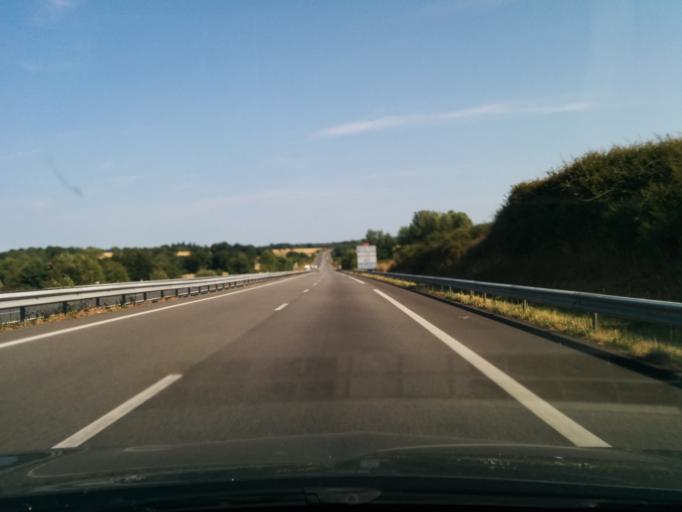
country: FR
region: Limousin
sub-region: Departement de la Haute-Vienne
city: Vicq-sur-Breuilh
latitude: 45.6683
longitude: 1.3859
